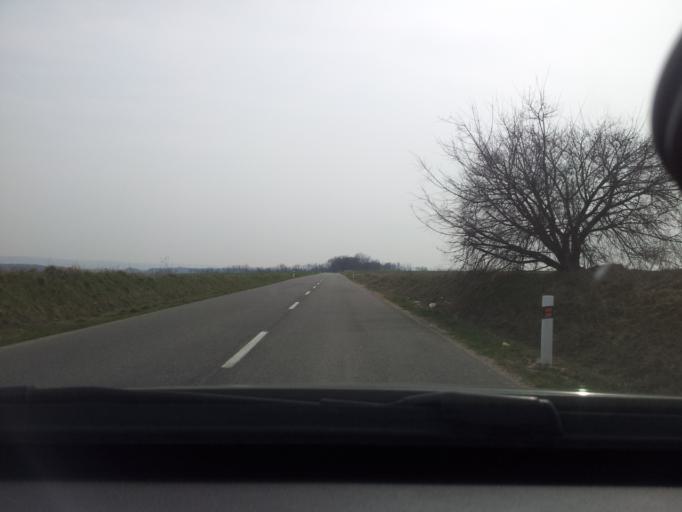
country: SK
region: Trnavsky
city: Leopoldov
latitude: 48.4640
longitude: 17.7023
